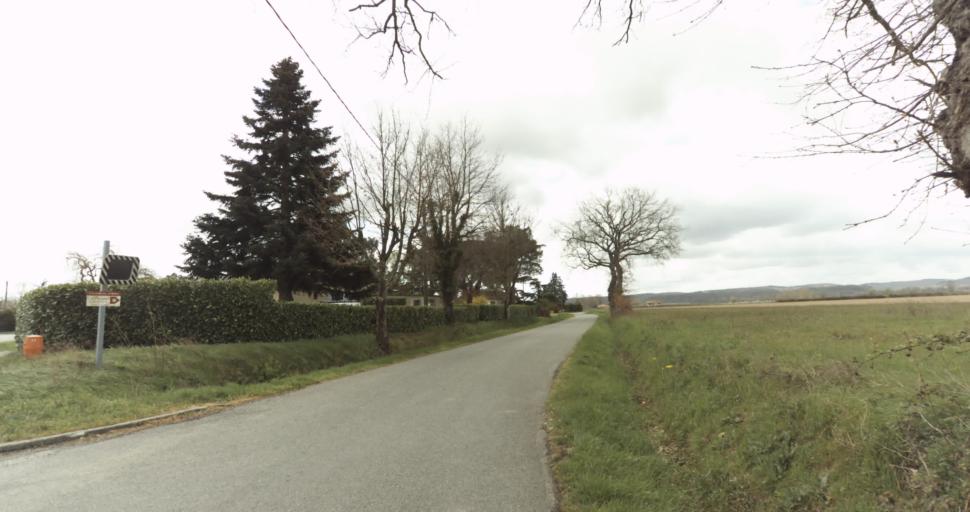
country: FR
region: Midi-Pyrenees
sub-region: Departement de la Haute-Garonne
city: Auterive
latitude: 43.3359
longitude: 1.4732
